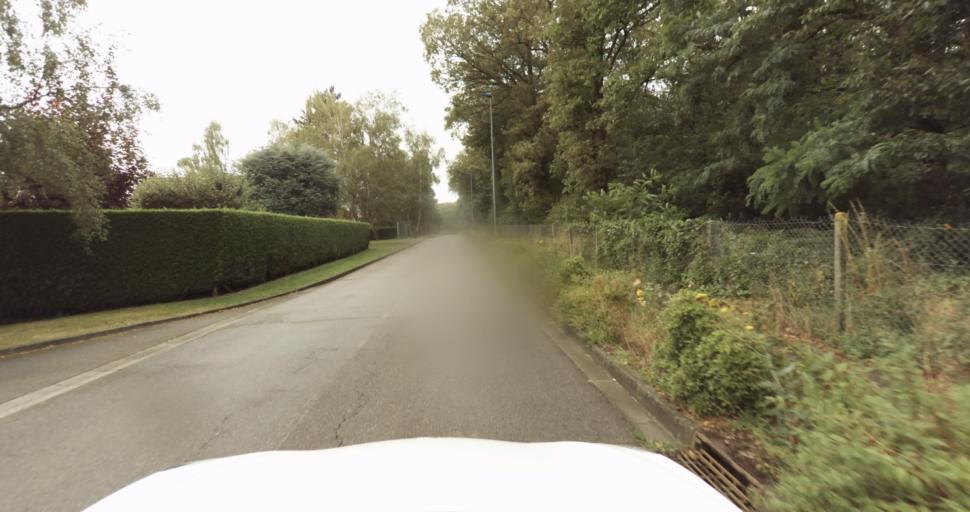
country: FR
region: Haute-Normandie
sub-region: Departement de l'Eure
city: Evreux
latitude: 49.0374
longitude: 1.1365
